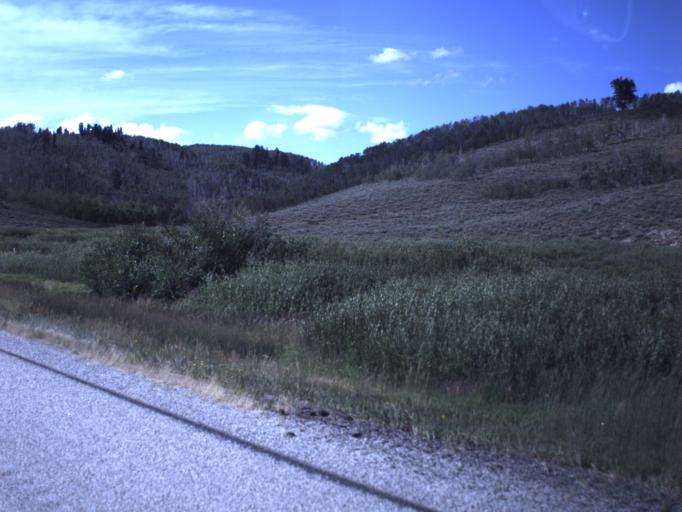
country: US
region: Utah
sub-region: Wasatch County
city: Heber
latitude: 40.2846
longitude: -111.2392
